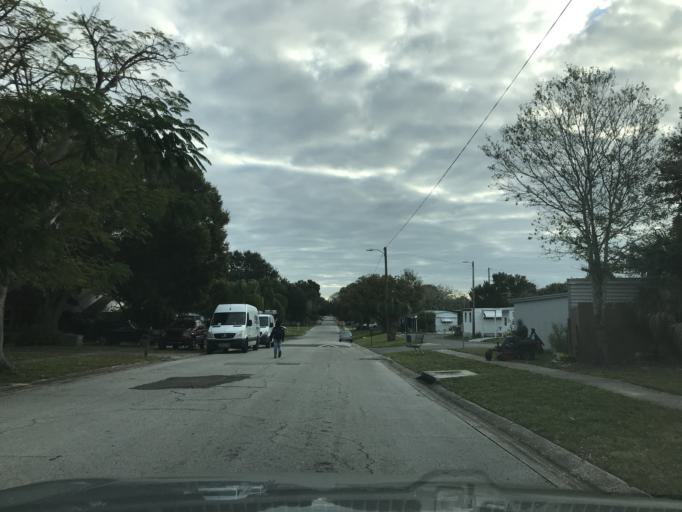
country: US
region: Florida
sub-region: Pinellas County
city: Clearwater
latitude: 27.9535
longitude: -82.7847
